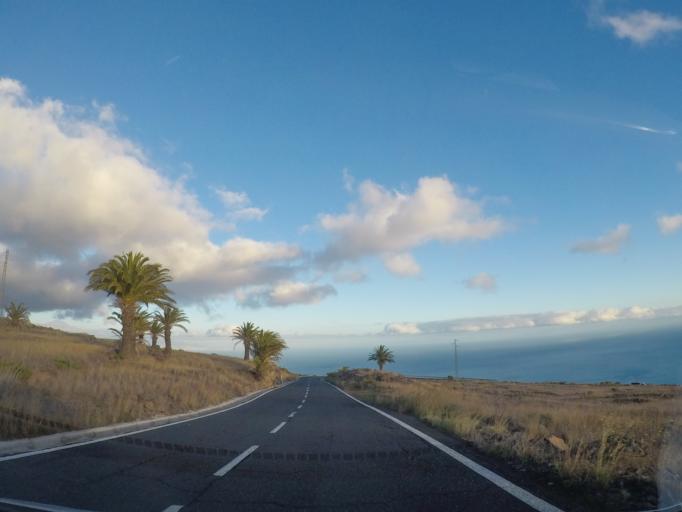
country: ES
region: Canary Islands
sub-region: Provincia de Santa Cruz de Tenerife
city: Alajero
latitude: 28.0482
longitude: -17.2312
